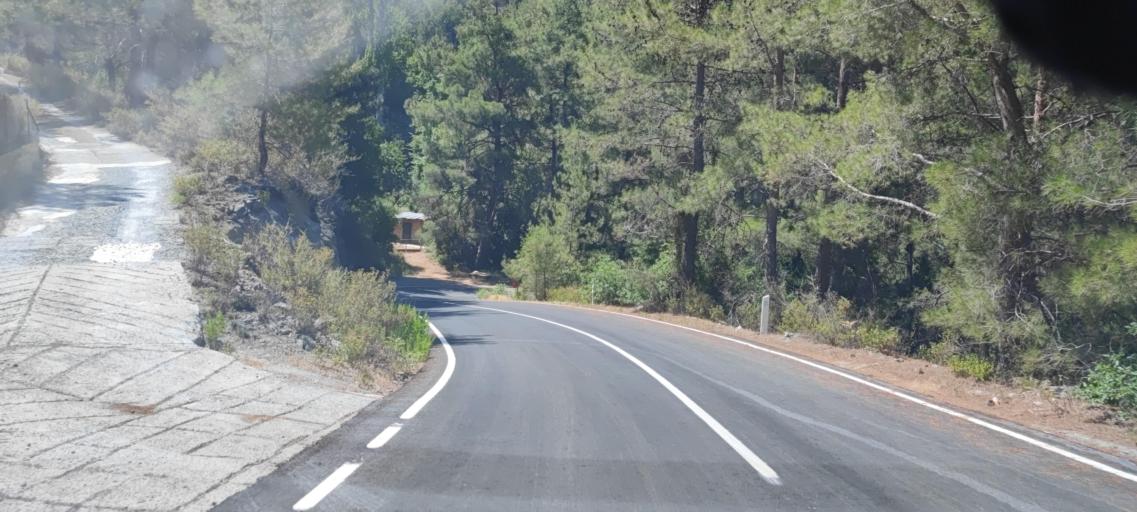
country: CY
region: Lefkosia
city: Kakopetria
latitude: 34.9210
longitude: 32.8096
